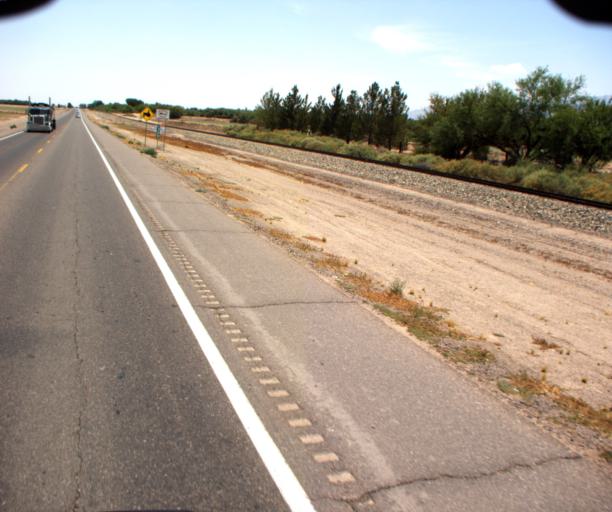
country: US
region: Arizona
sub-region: Graham County
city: Pima
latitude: 32.9095
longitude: -109.8515
